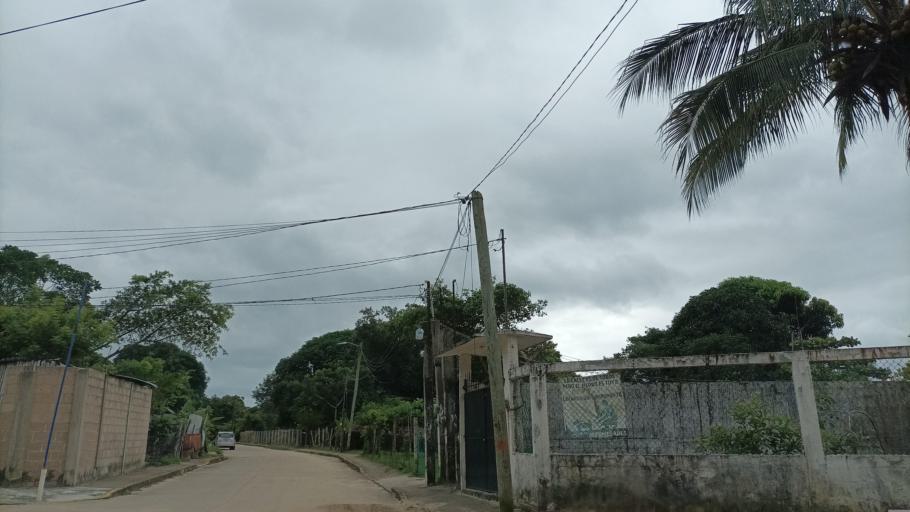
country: MX
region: Veracruz
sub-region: Cosoleacaque
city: Residencial las Olas
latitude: 18.0690
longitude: -94.5909
